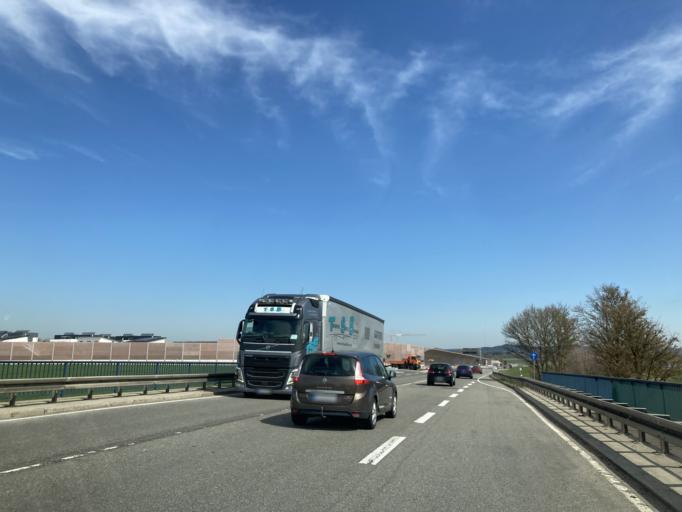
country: DE
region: Baden-Wuerttemberg
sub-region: Freiburg Region
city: Hufingen
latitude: 47.9206
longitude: 8.5050
